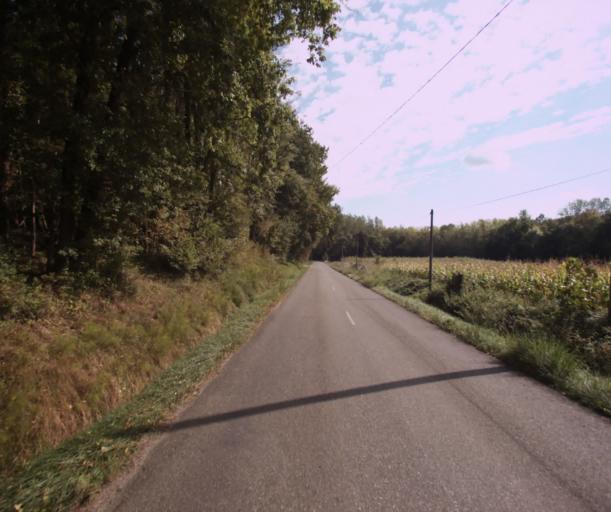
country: FR
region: Midi-Pyrenees
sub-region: Departement du Gers
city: Cazaubon
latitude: 43.9335
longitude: -0.0765
